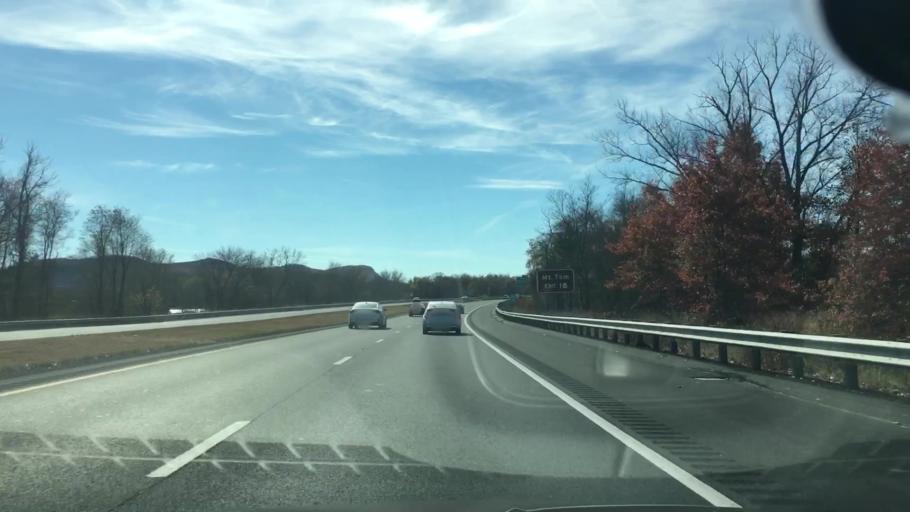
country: US
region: Massachusetts
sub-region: Hampshire County
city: Northampton
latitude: 42.3153
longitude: -72.6172
